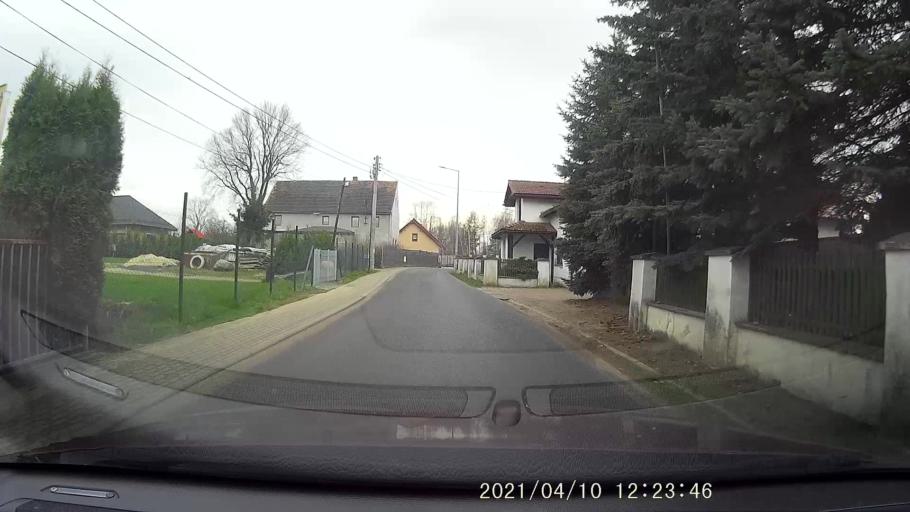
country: PL
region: Lower Silesian Voivodeship
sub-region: Powiat zgorzelecki
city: Lagow
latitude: 51.1634
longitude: 15.0242
